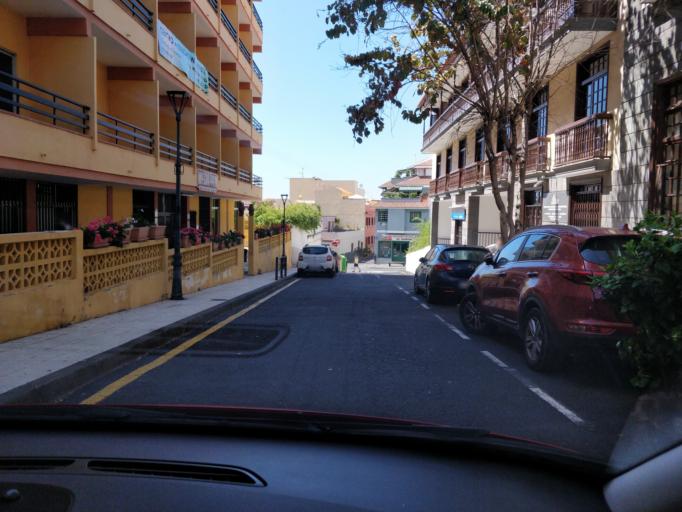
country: ES
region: Canary Islands
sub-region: Provincia de Santa Cruz de Tenerife
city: Puerto de la Cruz
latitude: 28.4158
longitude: -16.5538
